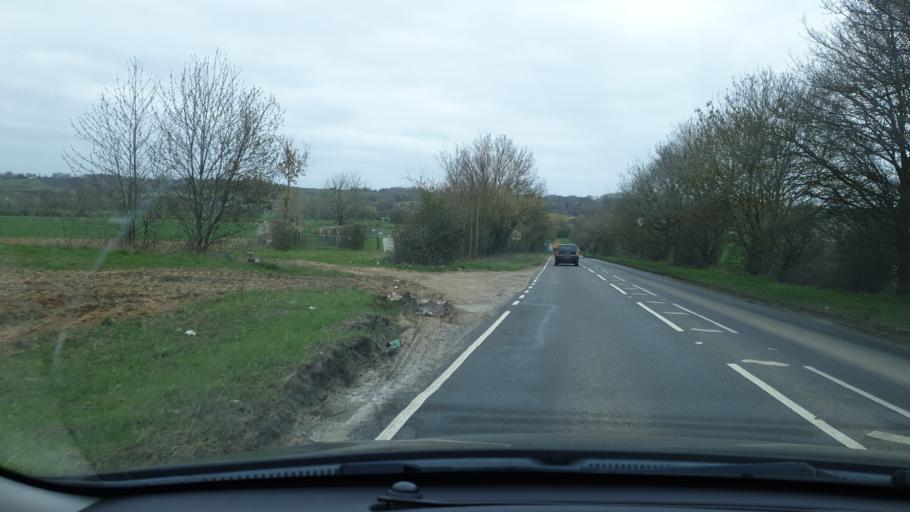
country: GB
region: England
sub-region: Essex
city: Great Horkesley
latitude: 51.9626
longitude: 0.8684
